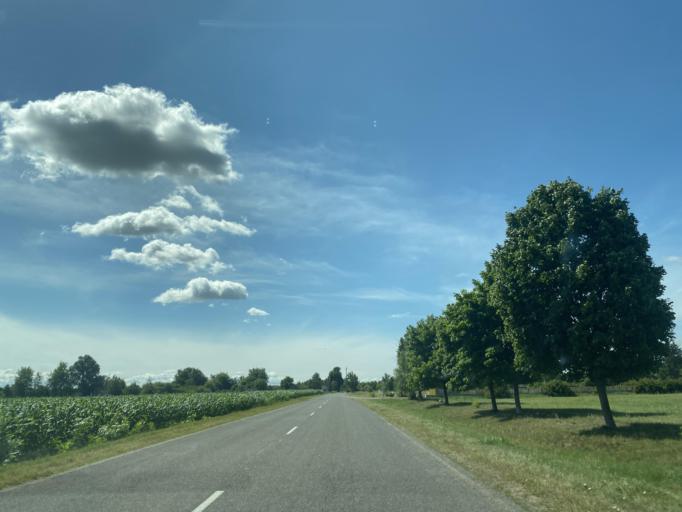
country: BY
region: Brest
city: Ivanava
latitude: 52.2104
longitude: 25.6291
